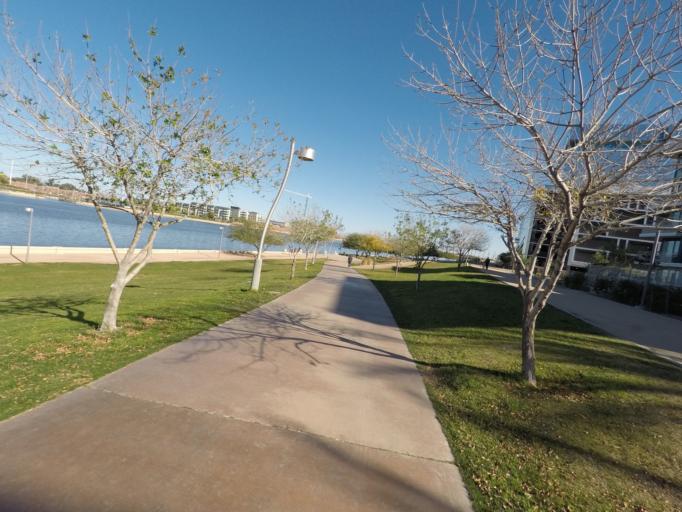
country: US
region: Arizona
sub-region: Maricopa County
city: Tempe Junction
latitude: 33.4318
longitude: -111.9355
